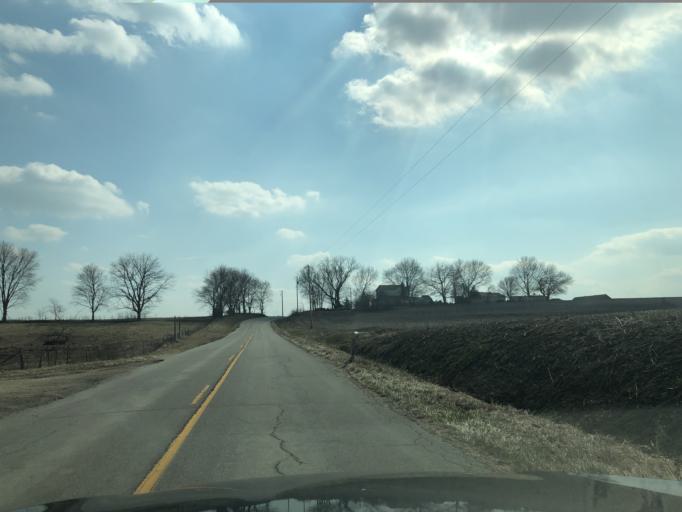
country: US
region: Missouri
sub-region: Platte County
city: Weston
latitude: 39.4579
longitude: -94.8461
